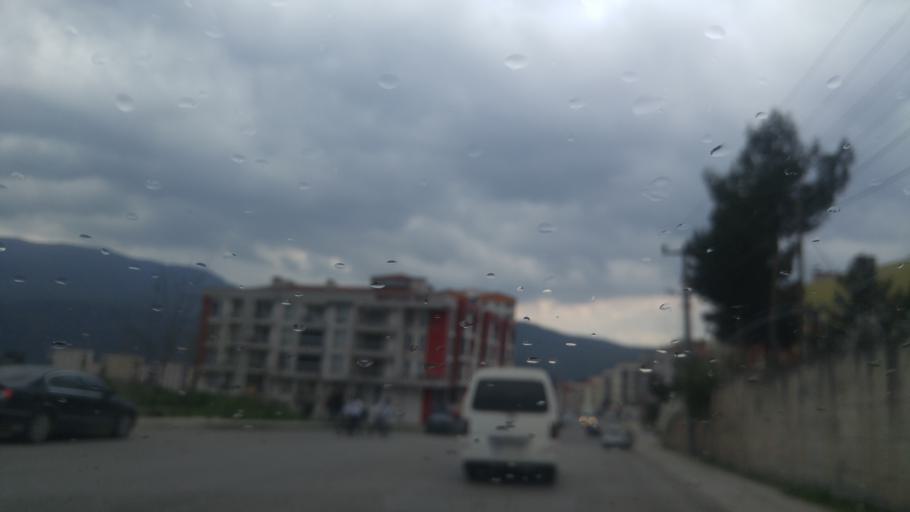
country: TR
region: Karabuk
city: Safranbolu
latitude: 41.2226
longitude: 32.6727
